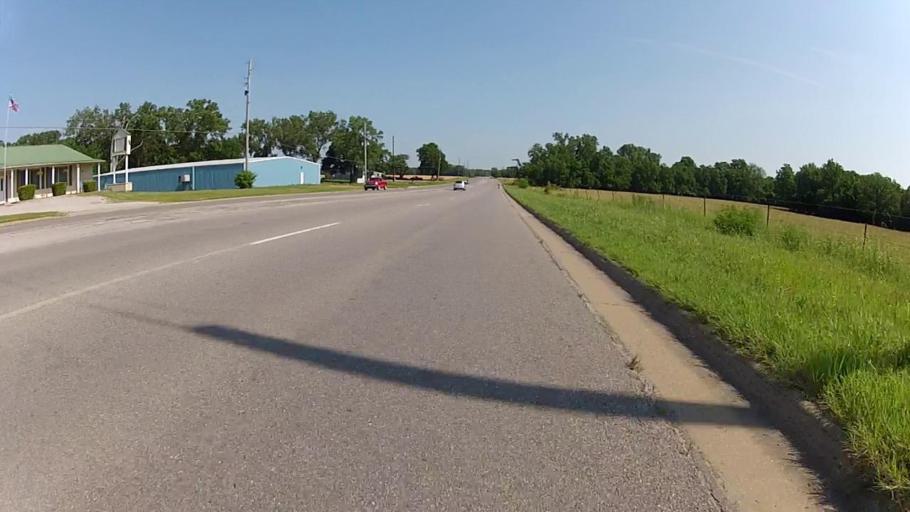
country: US
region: Kansas
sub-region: Montgomery County
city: Independence
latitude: 37.2063
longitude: -95.7106
